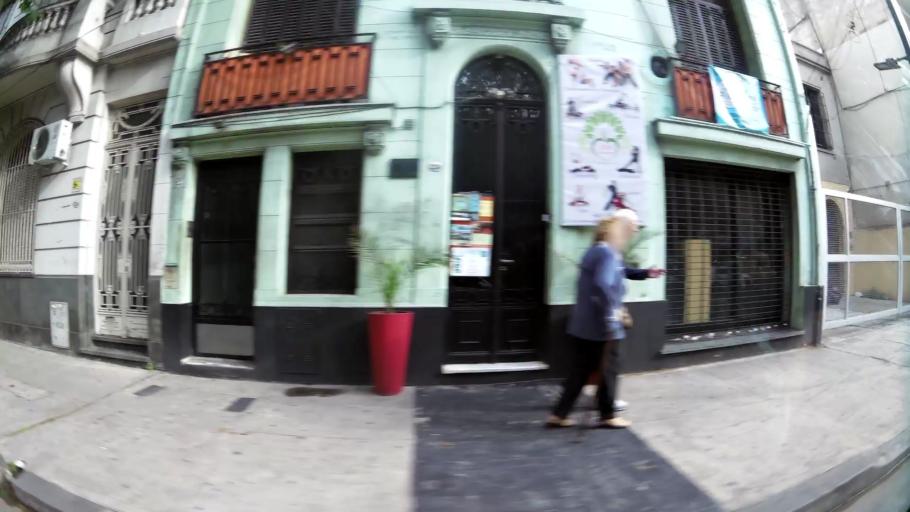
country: AR
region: Buenos Aires F.D.
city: Villa Santa Rita
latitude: -34.6304
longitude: -58.4595
